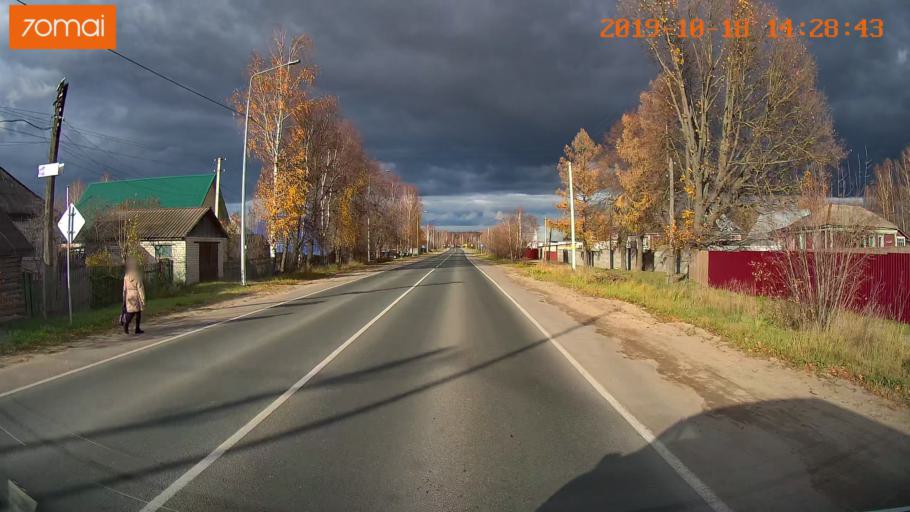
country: RU
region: Rjazan
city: Tuma
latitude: 55.1502
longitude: 40.5547
